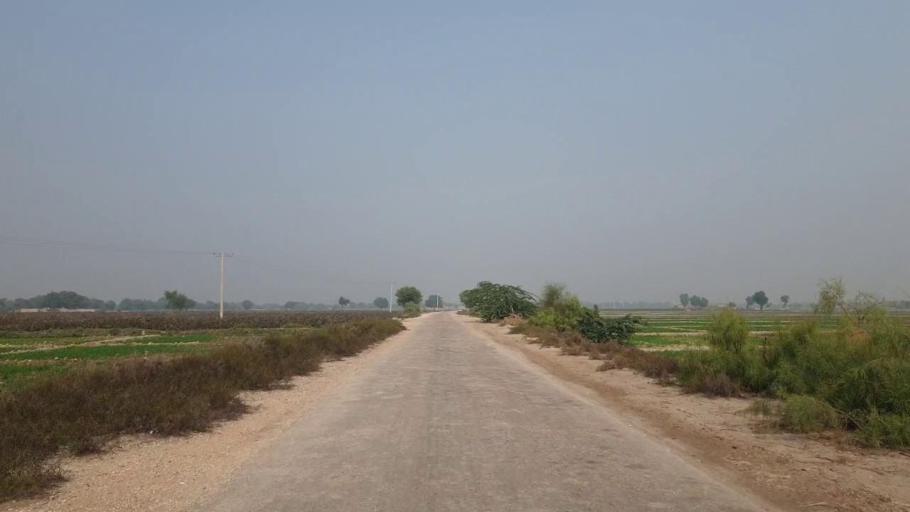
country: PK
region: Sindh
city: Bhan
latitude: 26.5260
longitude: 67.6930
